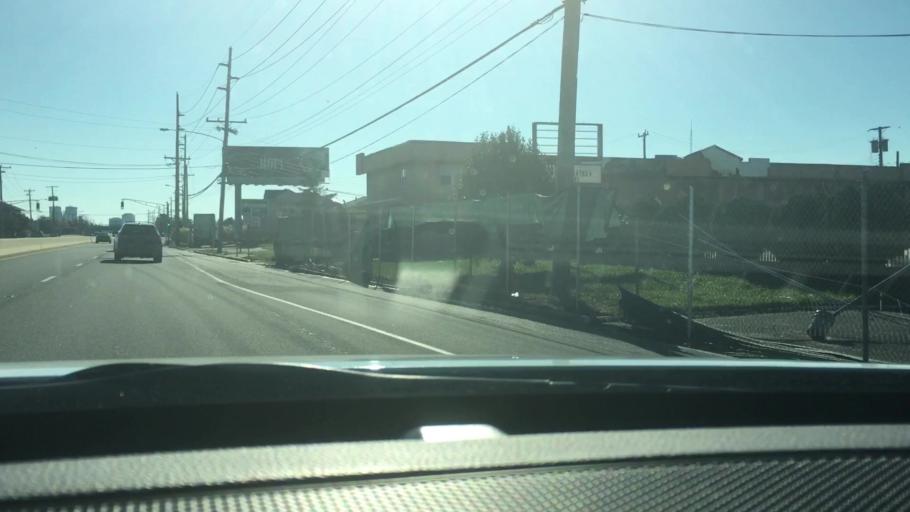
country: US
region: New Jersey
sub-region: Atlantic County
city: Ventnor City
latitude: 39.3719
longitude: -74.4790
